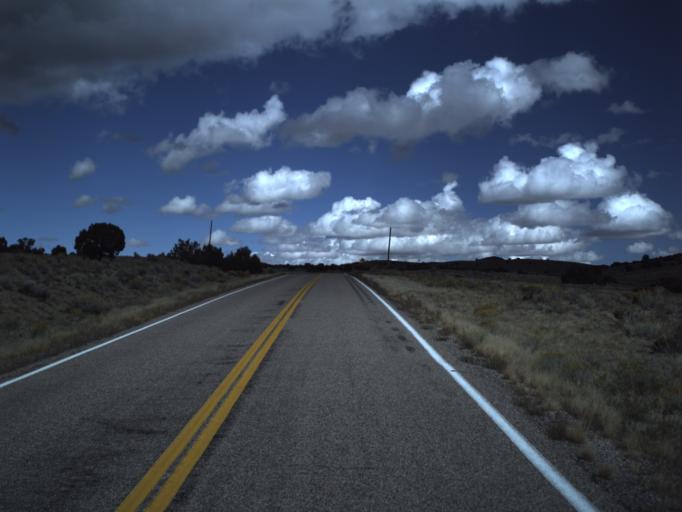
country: US
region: Utah
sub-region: Beaver County
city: Milford
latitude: 38.4471
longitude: -113.2620
